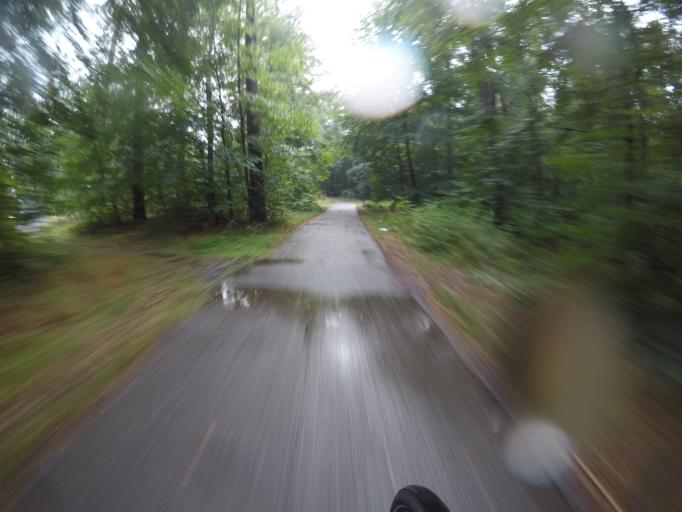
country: DE
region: Baden-Wuerttemberg
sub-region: Regierungsbezirk Stuttgart
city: Sindelfingen
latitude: 48.6918
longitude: 9.0397
